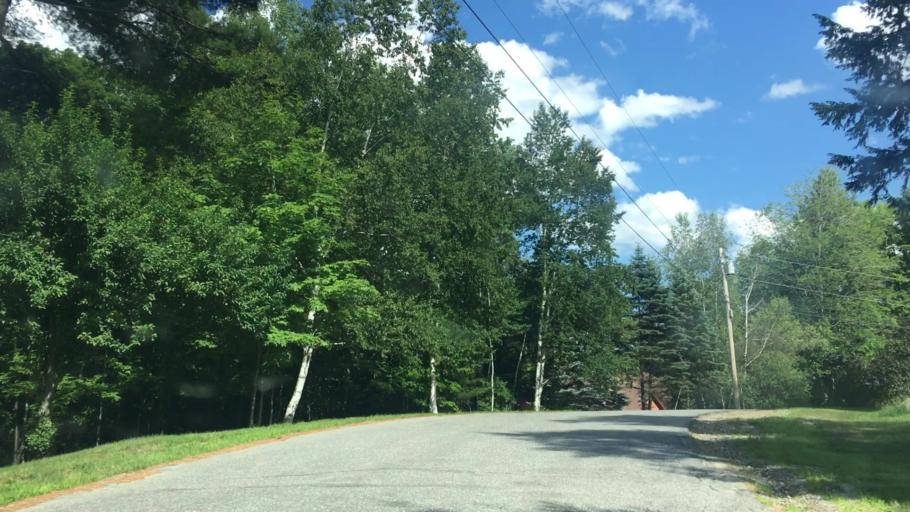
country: US
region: Maine
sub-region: Franklin County
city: Farmington
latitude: 44.6731
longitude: -70.1349
